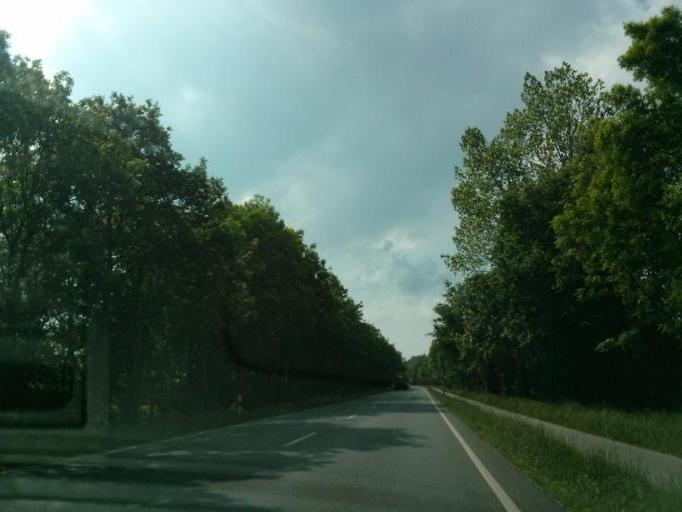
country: DE
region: Lower Saxony
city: Loxstedt
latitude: 53.4920
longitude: 8.6502
